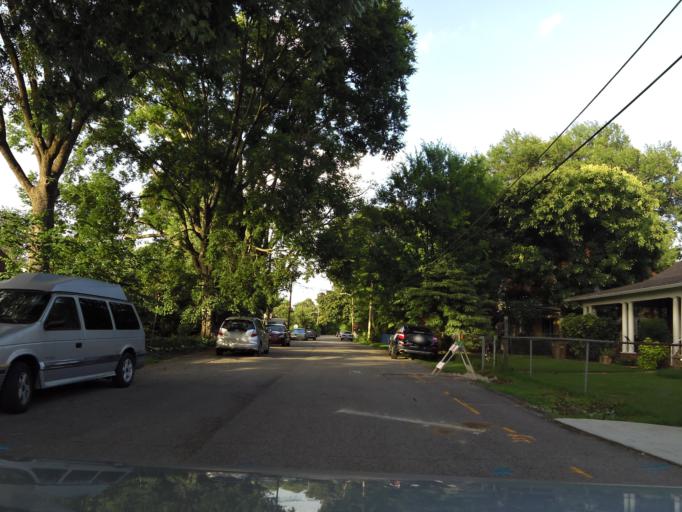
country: US
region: Tennessee
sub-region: Knox County
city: Knoxville
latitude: 35.9593
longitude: -83.9072
